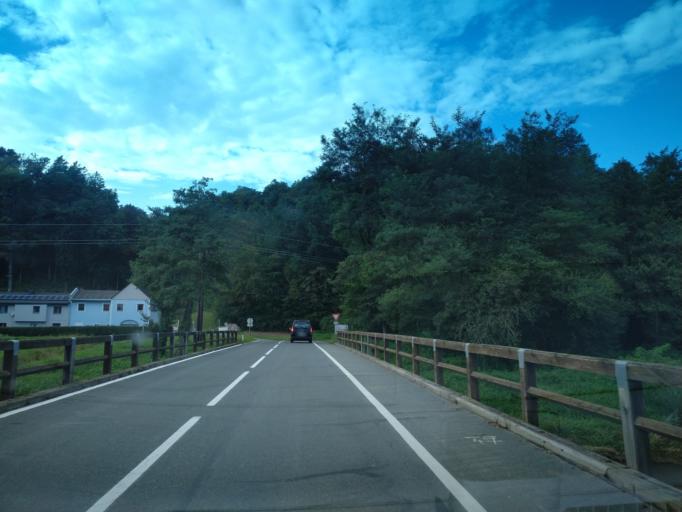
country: AT
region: Styria
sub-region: Politischer Bezirk Leibnitz
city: Kaindorf an der Sulm
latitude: 46.7908
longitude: 15.5240
